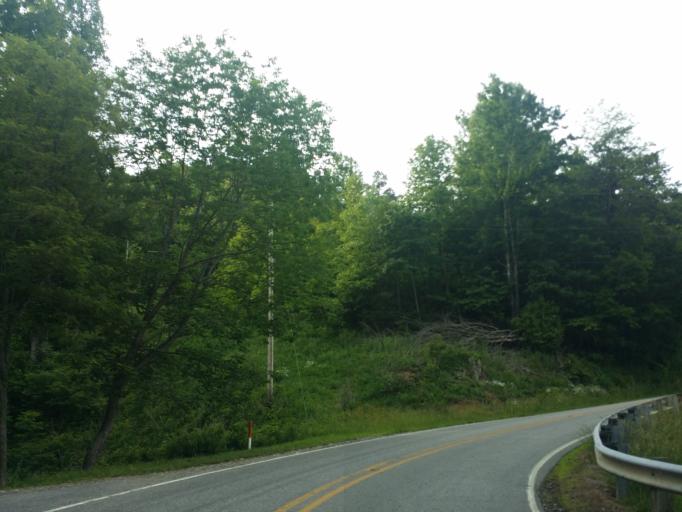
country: US
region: North Carolina
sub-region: Haywood County
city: West Canton
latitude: 35.6963
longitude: -82.8274
